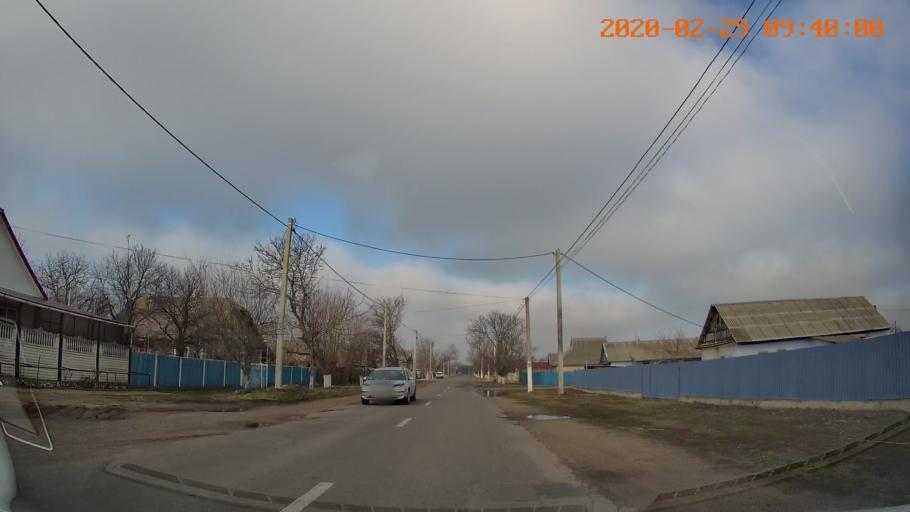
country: MD
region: Telenesti
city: Crasnoe
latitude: 46.6380
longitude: 29.8484
